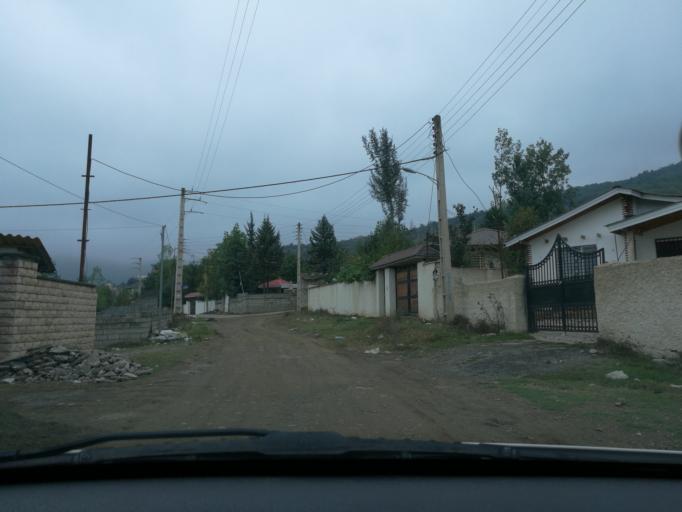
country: IR
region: Mazandaran
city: `Abbasabad
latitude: 36.5049
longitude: 51.1991
